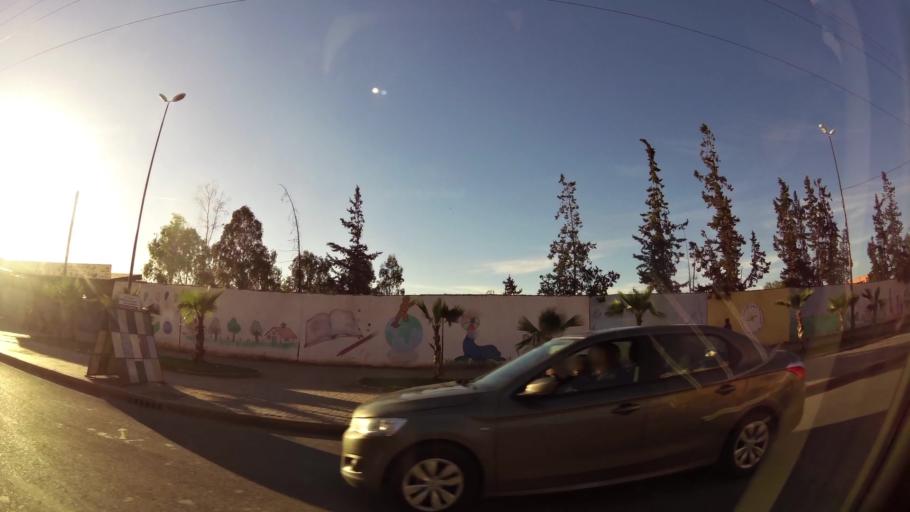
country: MA
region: Marrakech-Tensift-Al Haouz
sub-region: Marrakech
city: Marrakesh
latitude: 31.6188
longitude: -8.0535
